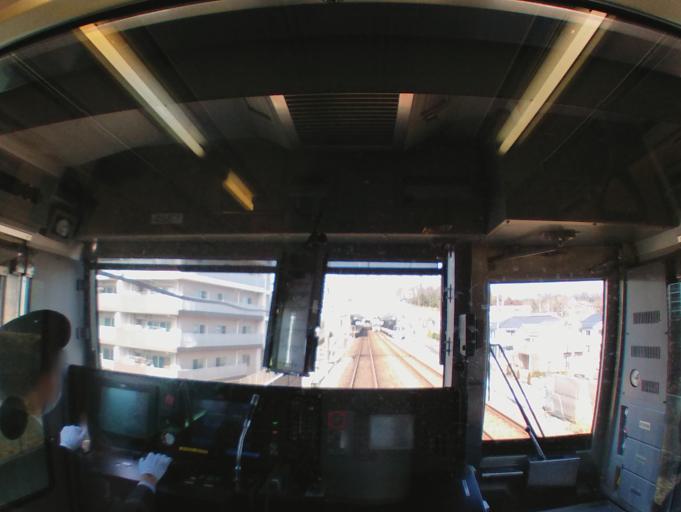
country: JP
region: Tokyo
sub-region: Machida-shi
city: Machida
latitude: 35.6151
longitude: 139.4687
